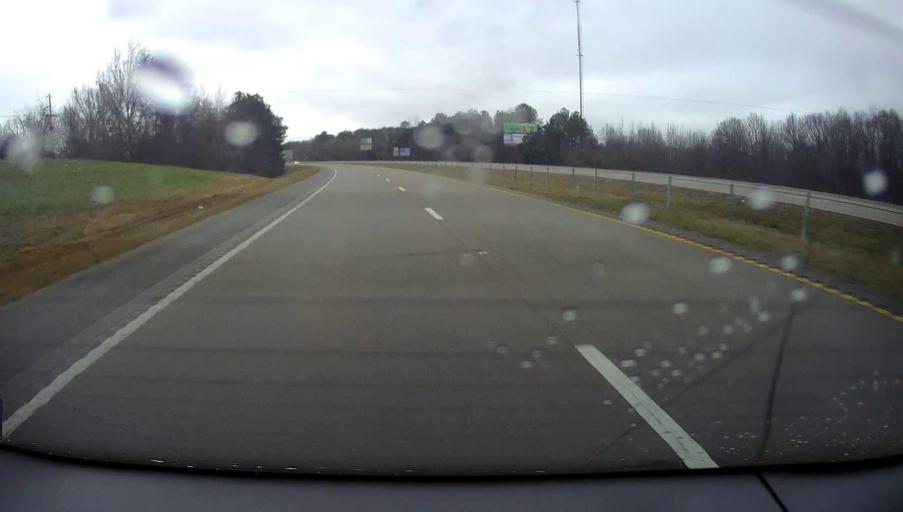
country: US
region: Mississippi
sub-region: Alcorn County
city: Corinth
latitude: 34.9182
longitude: -88.5422
